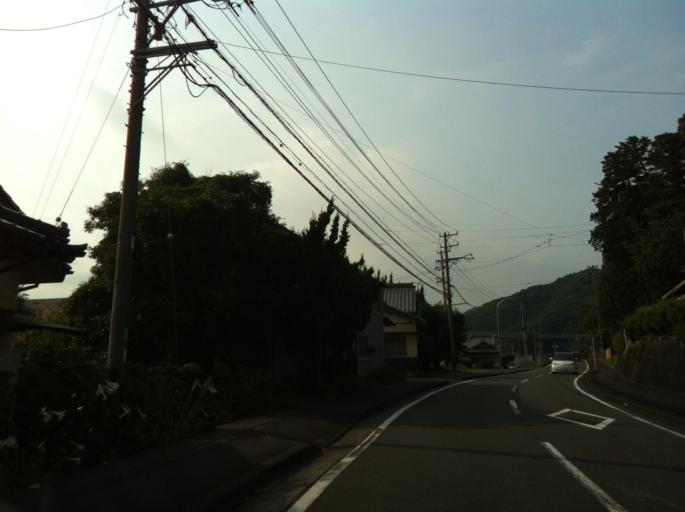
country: JP
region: Shizuoka
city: Fujieda
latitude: 34.9135
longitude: 138.2697
